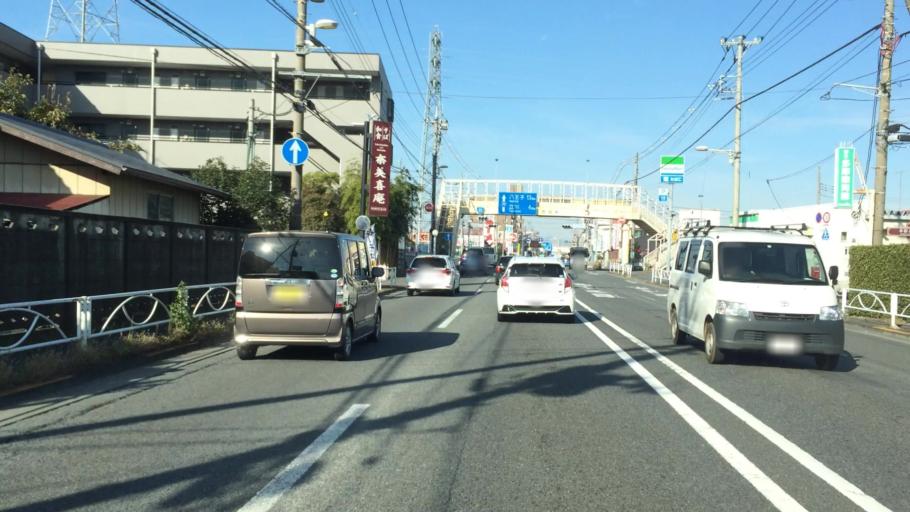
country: JP
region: Tokyo
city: Kokubunji
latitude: 35.6758
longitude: 139.4535
